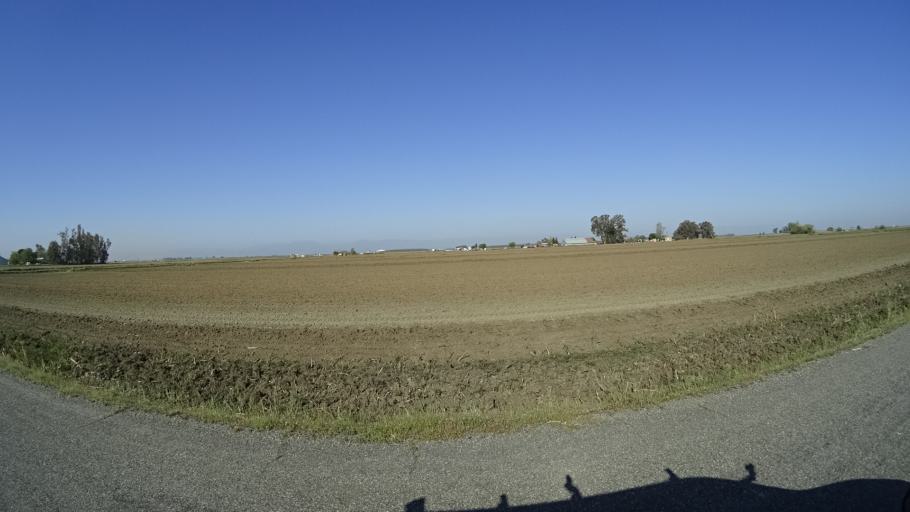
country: US
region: California
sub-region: Glenn County
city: Willows
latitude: 39.5724
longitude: -122.1074
